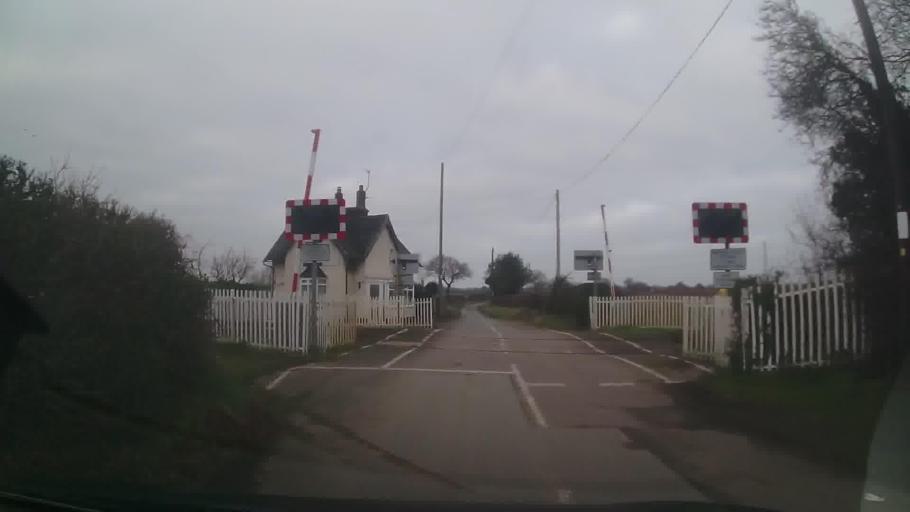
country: GB
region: England
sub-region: Shropshire
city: Petton
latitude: 52.7948
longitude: -2.8410
